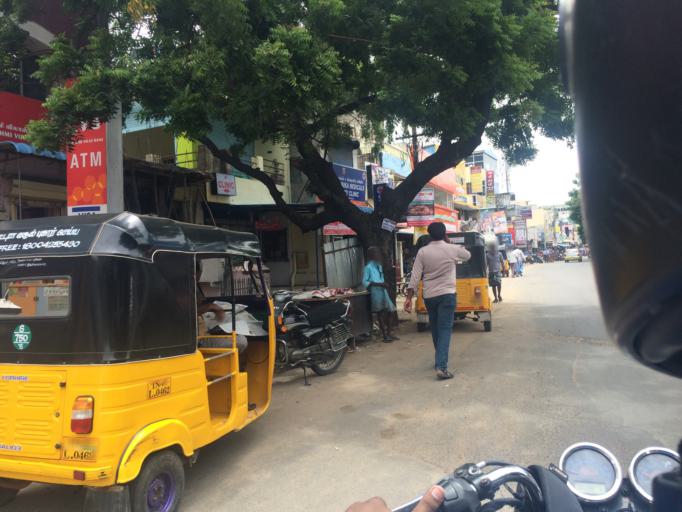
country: IN
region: Tamil Nadu
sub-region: Kancheepuram
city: Alandur
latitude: 12.9861
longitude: 80.2229
